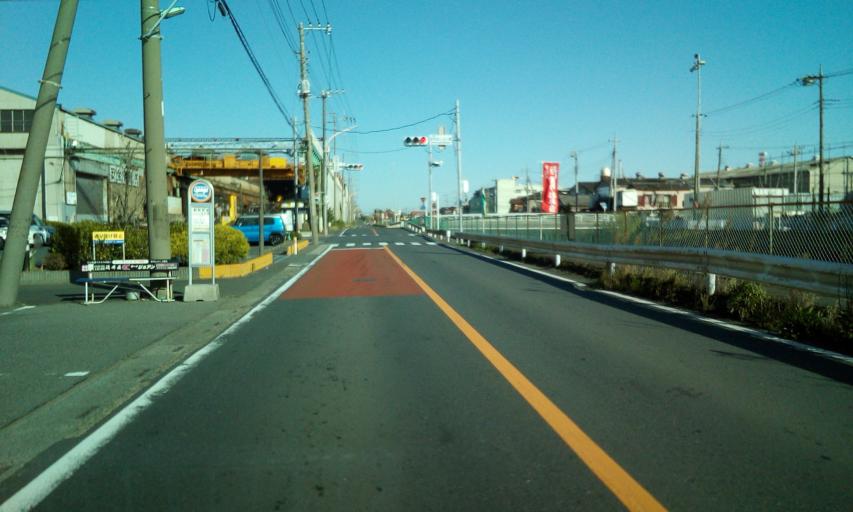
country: JP
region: Chiba
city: Matsudo
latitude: 35.8121
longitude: 139.8837
